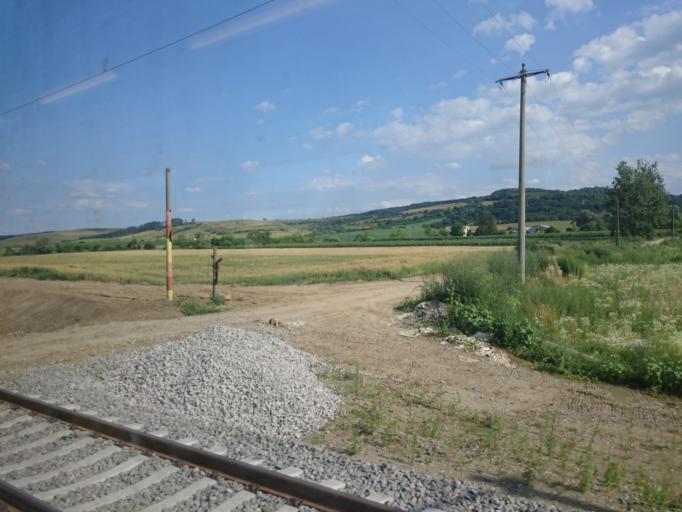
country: RO
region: Sibiu
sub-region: Comuna Laslea
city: Laslea
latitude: 46.2219
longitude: 24.6677
